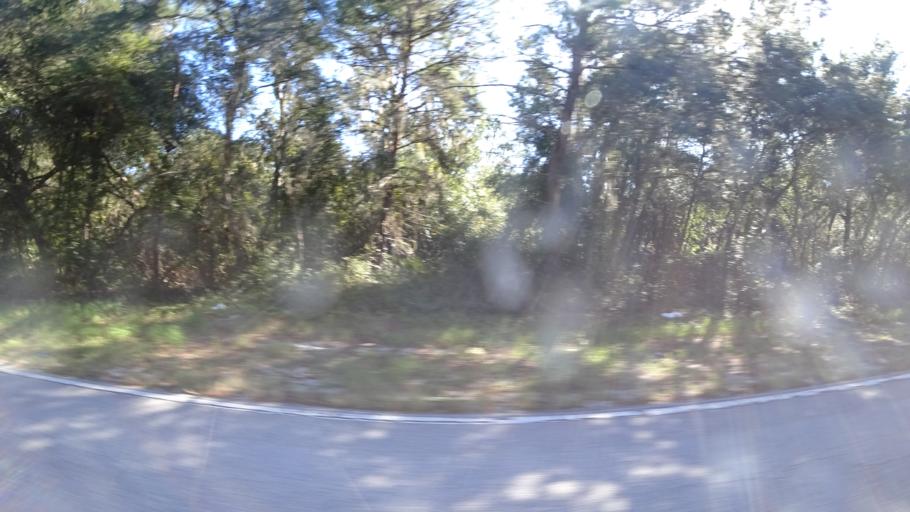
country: US
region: Florida
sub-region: Hillsborough County
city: Wimauma
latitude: 27.6577
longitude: -82.2942
